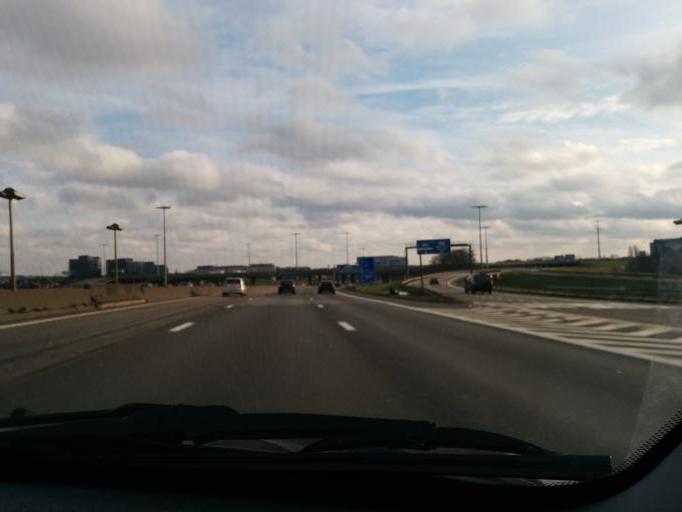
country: BE
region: Flanders
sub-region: Provincie Vlaams-Brabant
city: Diegem
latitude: 50.8951
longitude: 4.4489
